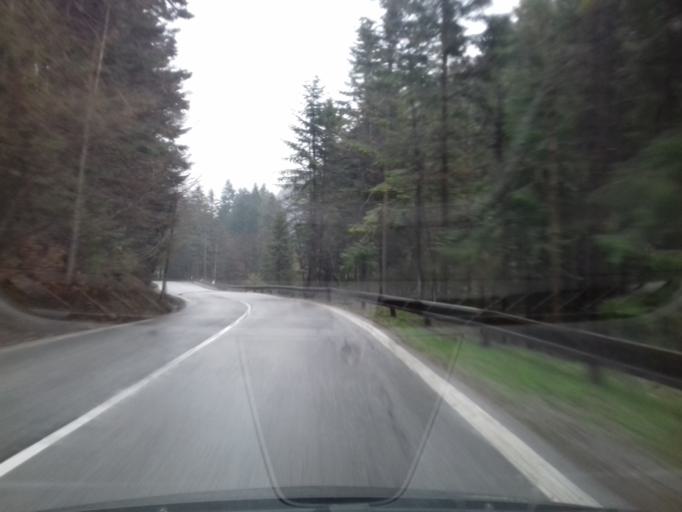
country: PL
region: Lesser Poland Voivodeship
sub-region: Powiat nowosadecki
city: Piwniczna-Zdroj
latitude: 49.3900
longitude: 20.6982
